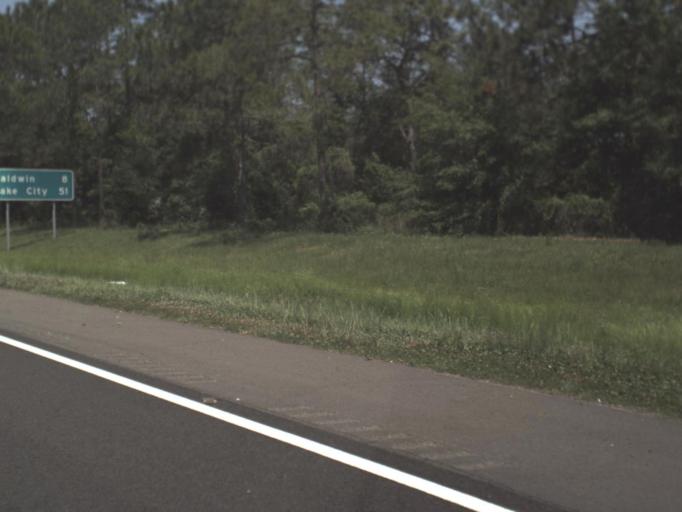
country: US
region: Florida
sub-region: Duval County
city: Baldwin
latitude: 30.3083
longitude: -81.8623
